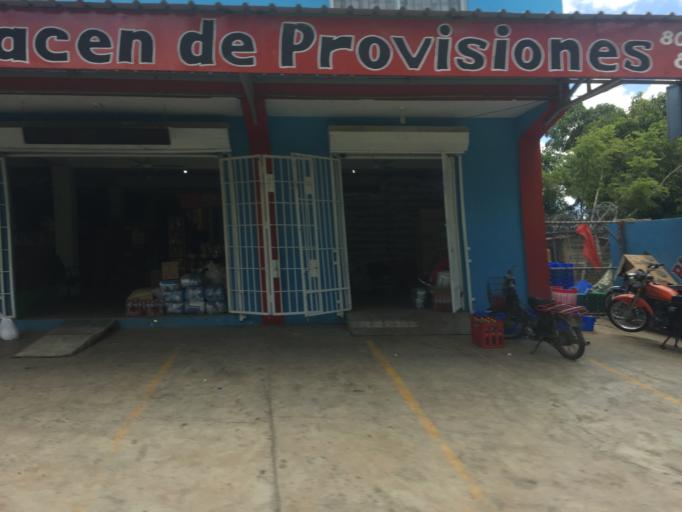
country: DO
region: Santiago
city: Tamboril
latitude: 19.4904
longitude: -70.6561
